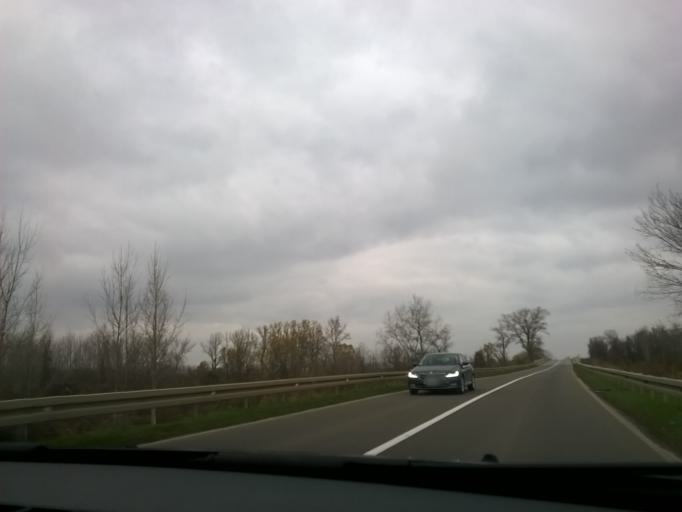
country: RS
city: Centa
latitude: 45.0950
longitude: 20.3755
